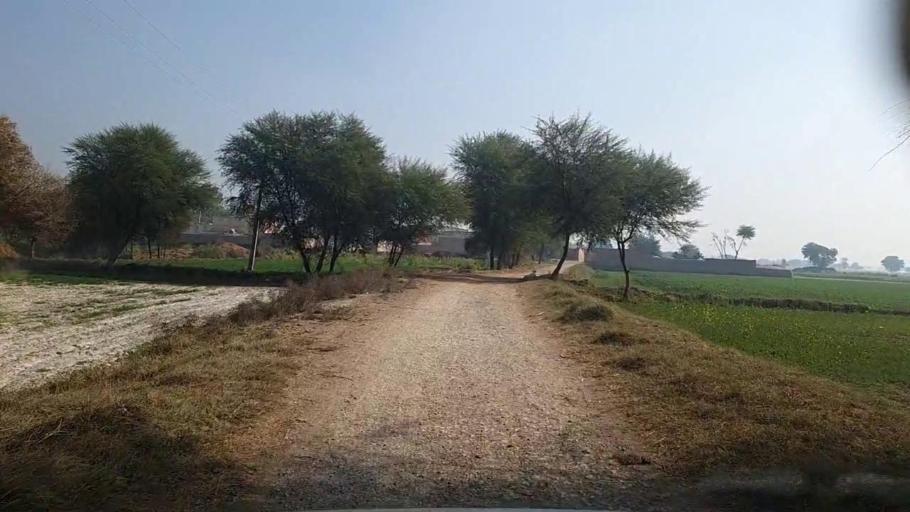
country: PK
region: Sindh
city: Khairpur
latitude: 27.9425
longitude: 69.6760
